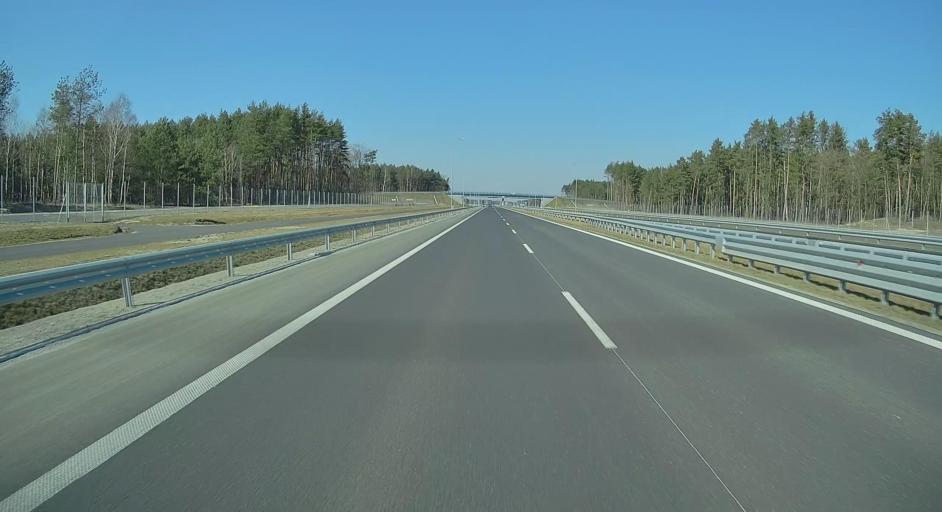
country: PL
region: Subcarpathian Voivodeship
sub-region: Powiat nizanski
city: Jezowe
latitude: 50.3821
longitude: 22.1675
